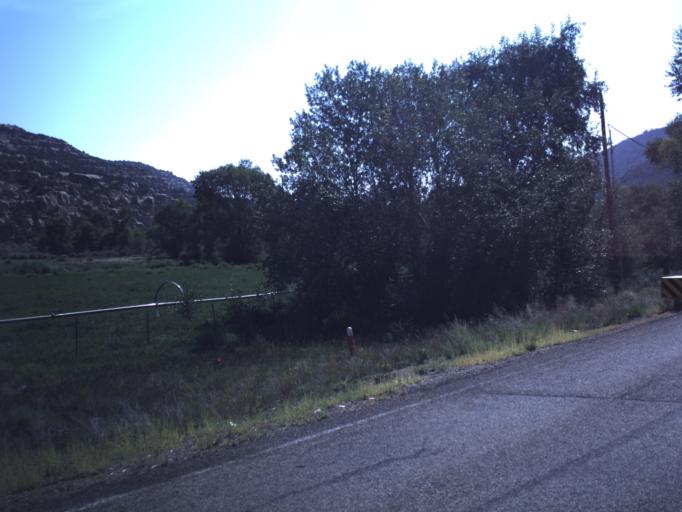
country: US
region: Utah
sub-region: Duchesne County
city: Duchesne
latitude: 40.3001
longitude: -110.6043
